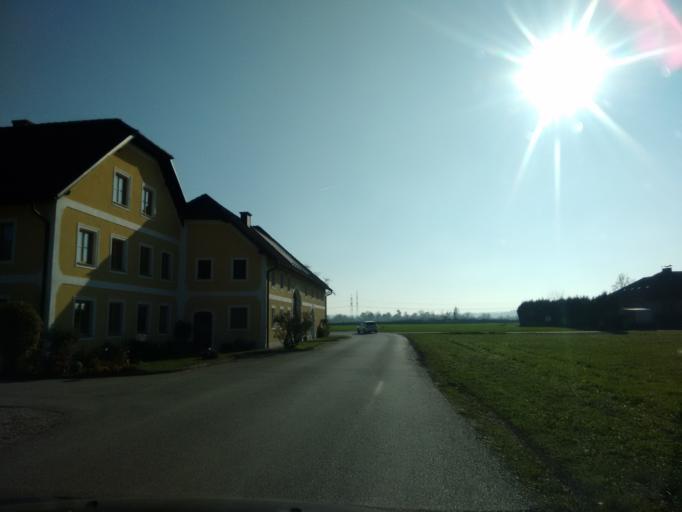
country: AT
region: Upper Austria
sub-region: Wels-Land
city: Gunskirchen
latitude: 48.1614
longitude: 13.9657
